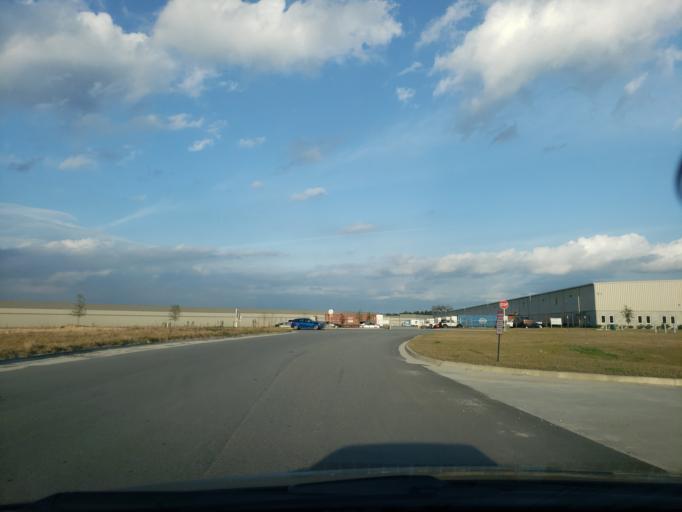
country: US
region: Georgia
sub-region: Chatham County
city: Bloomingdale
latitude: 32.1623
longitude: -81.2694
